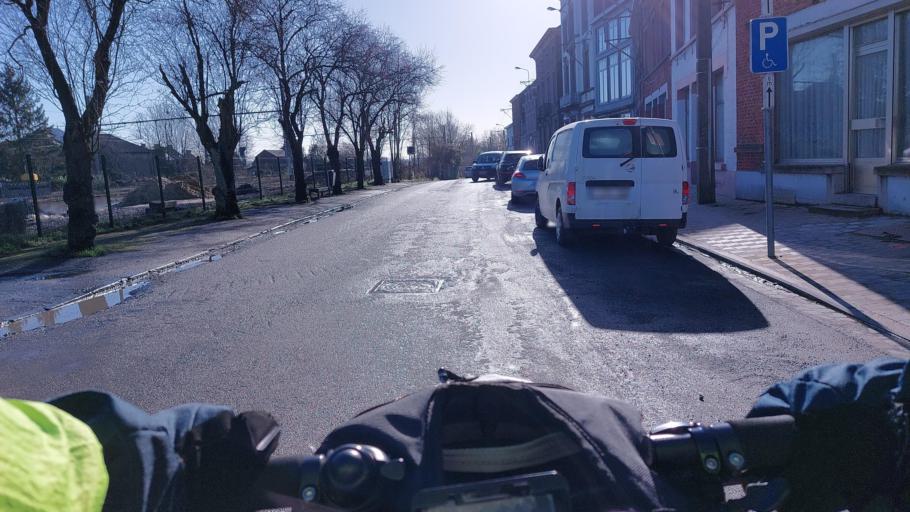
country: BE
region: Wallonia
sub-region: Province du Hainaut
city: Ecaussinnes-d'Enghien
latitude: 50.5617
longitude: 4.1567
